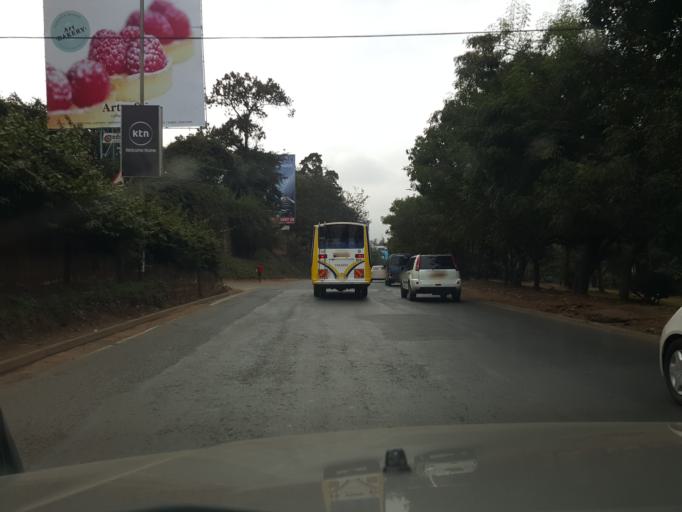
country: KE
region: Nairobi Area
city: Nairobi
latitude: -1.2666
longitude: 36.8039
